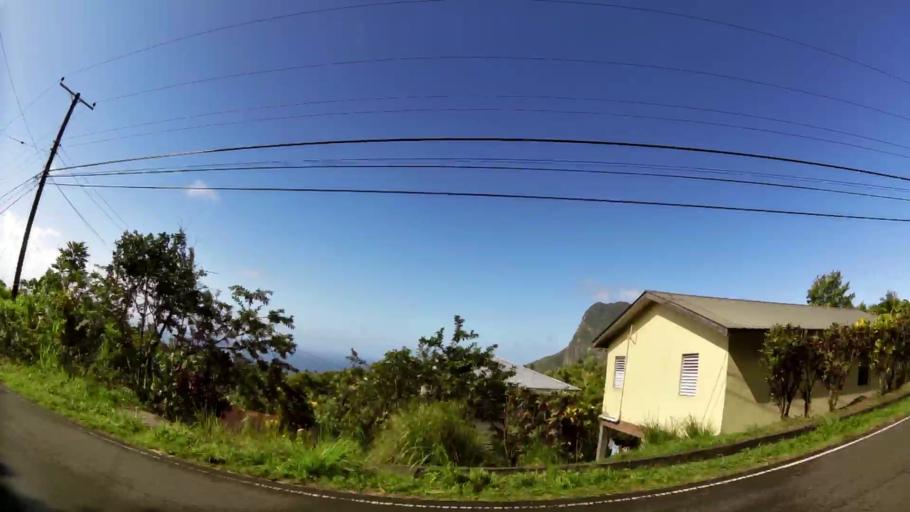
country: LC
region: Choiseul Quarter
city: Choiseul
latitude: 13.8098
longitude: -61.0397
